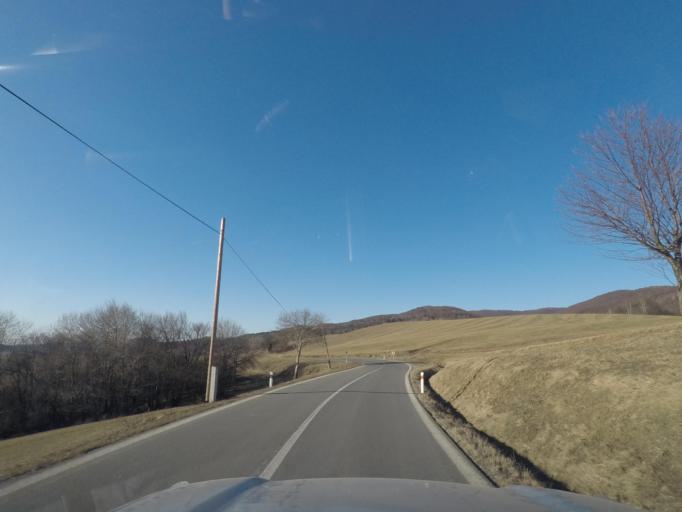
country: SK
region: Presovsky
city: Medzilaborce
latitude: 49.2141
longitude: 21.9849
